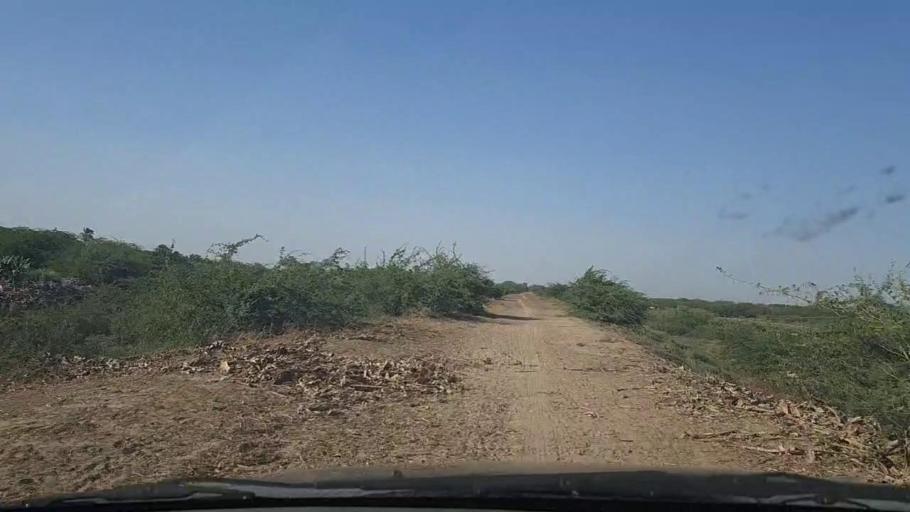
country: PK
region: Sindh
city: Chuhar Jamali
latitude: 24.3269
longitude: 67.7546
